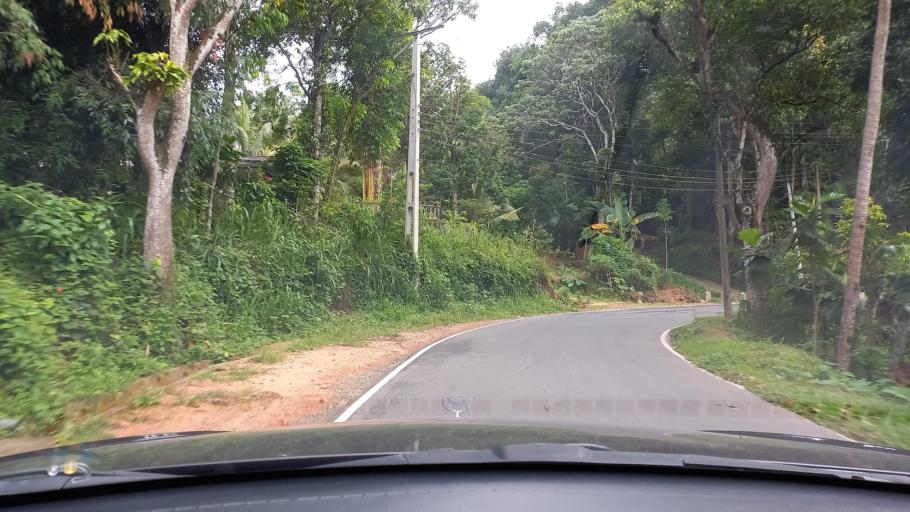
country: LK
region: Central
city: Gampola
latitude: 7.2174
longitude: 80.6122
